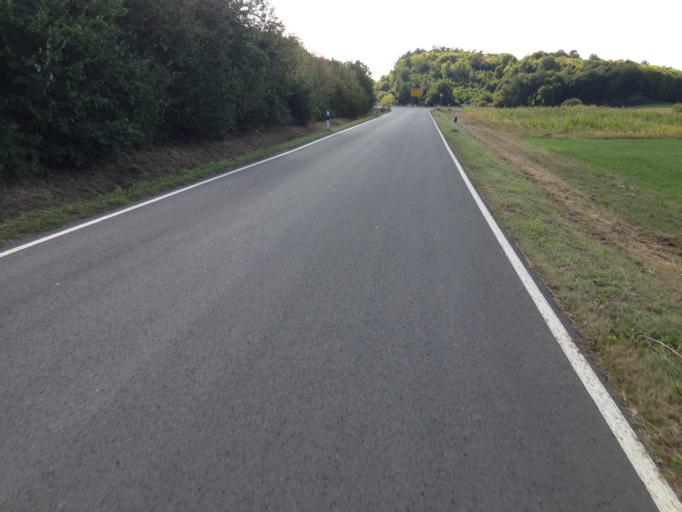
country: DE
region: Hesse
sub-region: Regierungsbezirk Giessen
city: Reiskirchen
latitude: 50.6127
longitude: 8.8604
